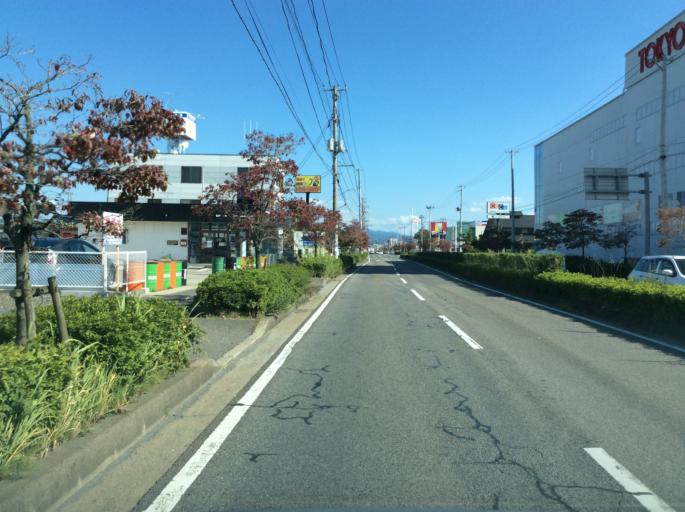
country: JP
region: Fukushima
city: Koriyama
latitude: 37.3698
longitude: 140.3532
